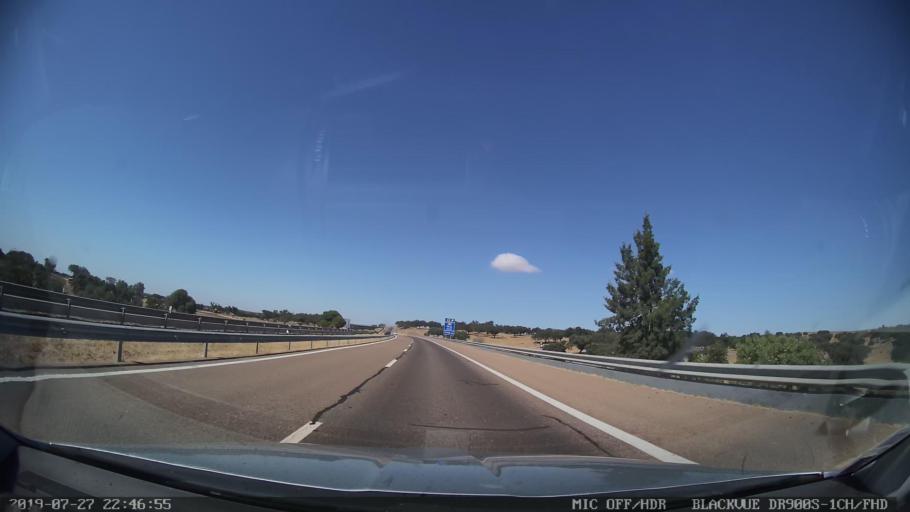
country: PT
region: Portalegre
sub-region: Elvas
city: Elvas
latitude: 38.9016
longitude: -7.1995
